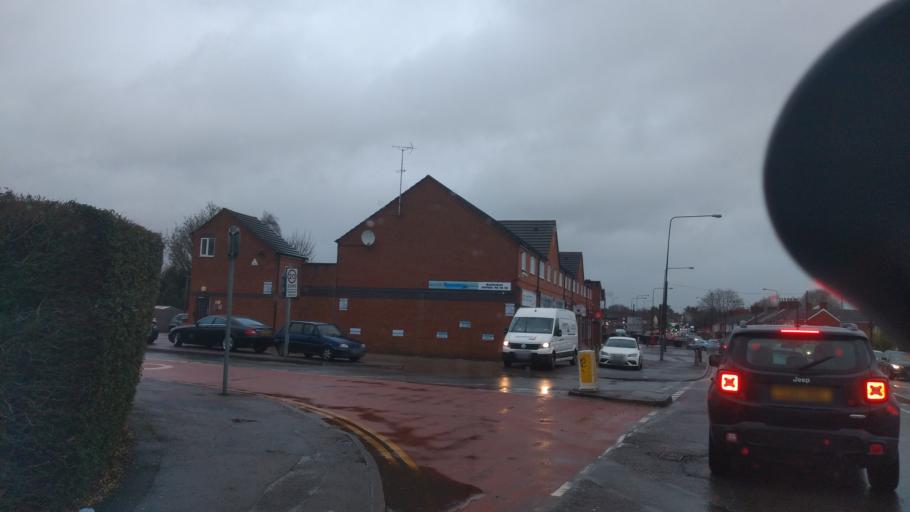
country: GB
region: England
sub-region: Borough of Swindon
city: Swindon
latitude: 51.5832
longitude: -1.7752
